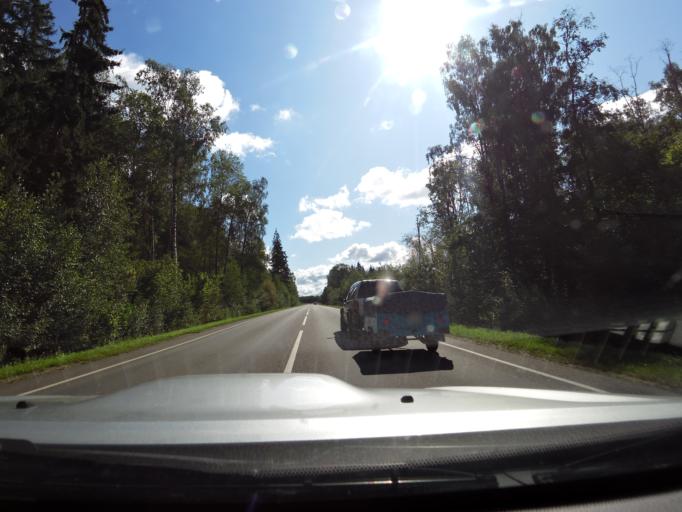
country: LT
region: Utenos apskritis
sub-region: Utena
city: Utena
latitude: 55.4869
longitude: 25.6333
